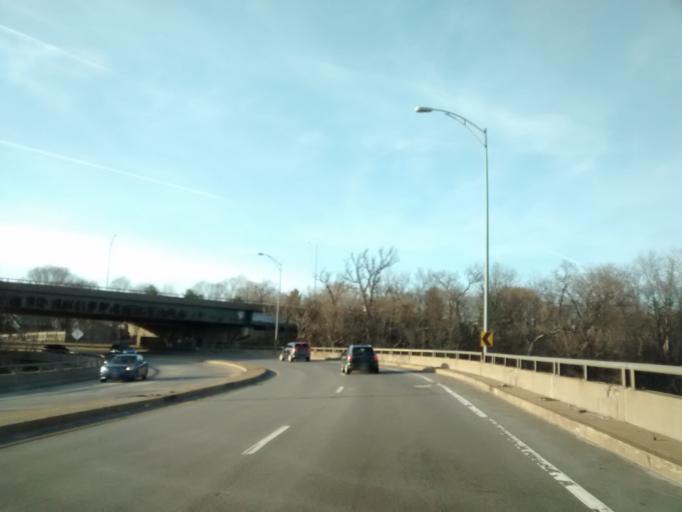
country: US
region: Massachusetts
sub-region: Middlesex County
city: Waltham
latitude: 42.3407
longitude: -71.2597
